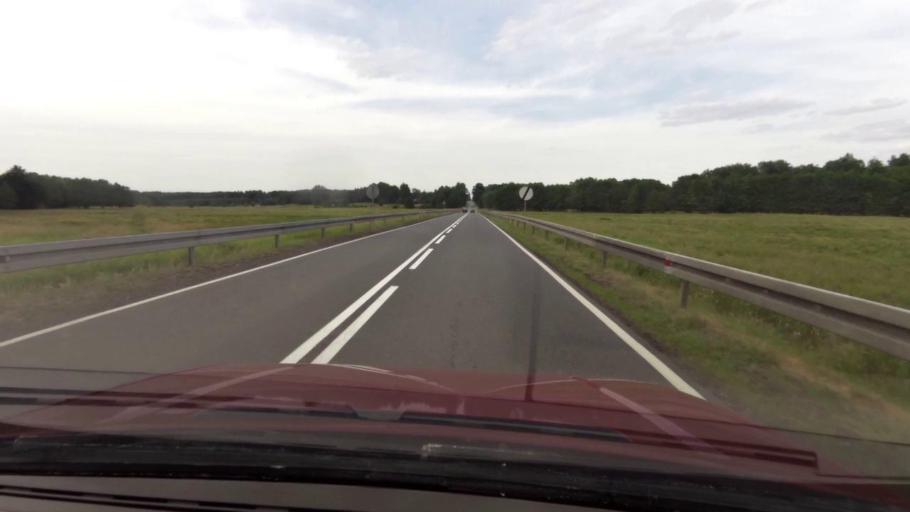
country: PL
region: Pomeranian Voivodeship
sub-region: Powiat bytowski
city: Trzebielino
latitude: 54.2314
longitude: 17.0874
